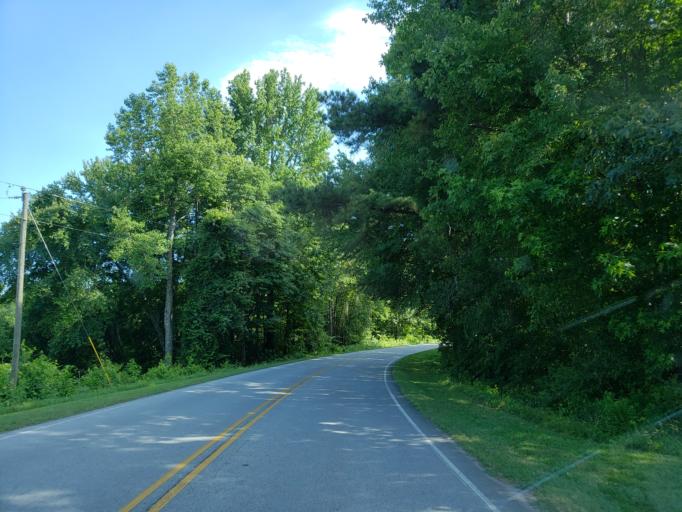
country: US
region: Georgia
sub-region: Haralson County
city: Buchanan
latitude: 33.8342
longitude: -85.0958
